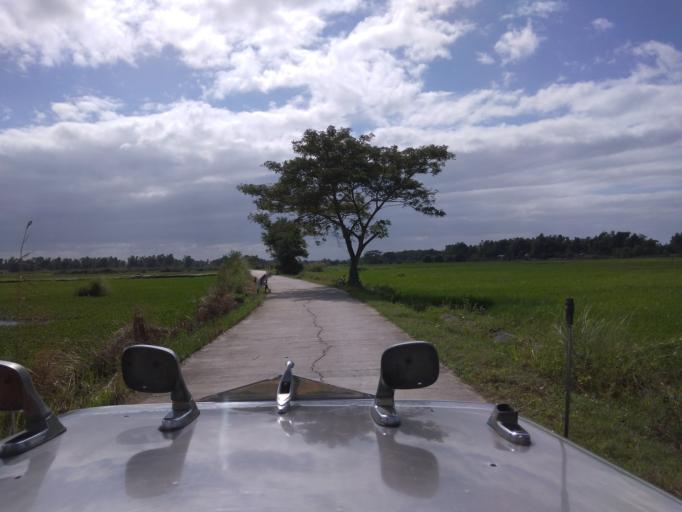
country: PH
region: Central Luzon
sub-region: Province of Pampanga
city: San Patricio
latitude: 15.0870
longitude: 120.7179
